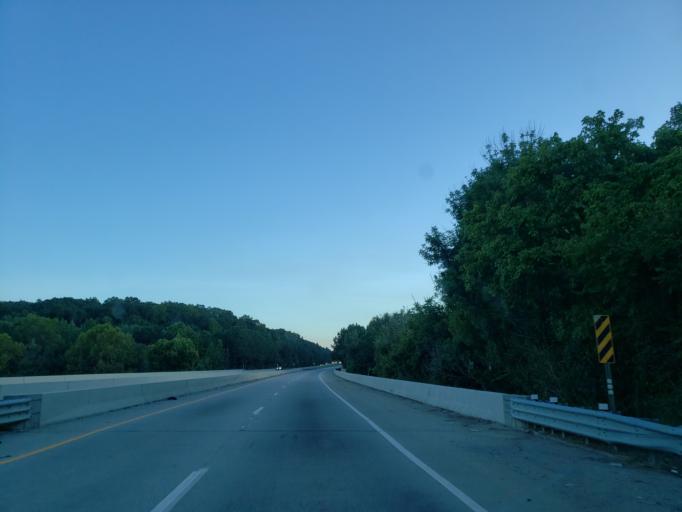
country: US
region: Georgia
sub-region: Floyd County
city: Rome
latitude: 34.2331
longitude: -85.1166
